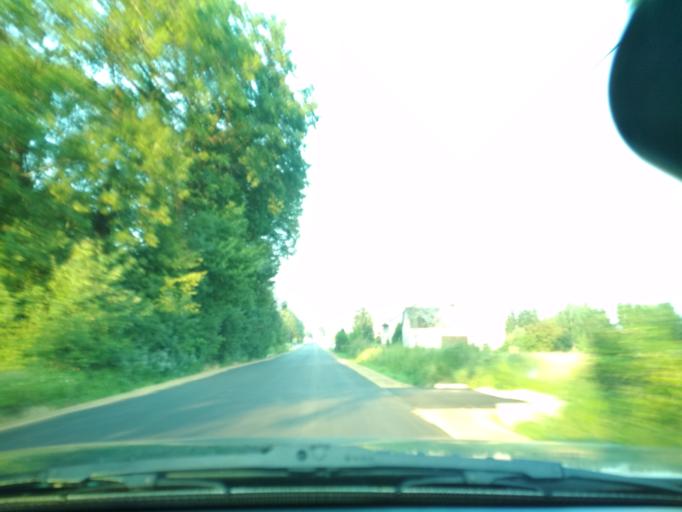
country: PL
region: Lesser Poland Voivodeship
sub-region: Powiat olkuski
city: Wolbrom
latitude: 50.4079
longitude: 19.7884
